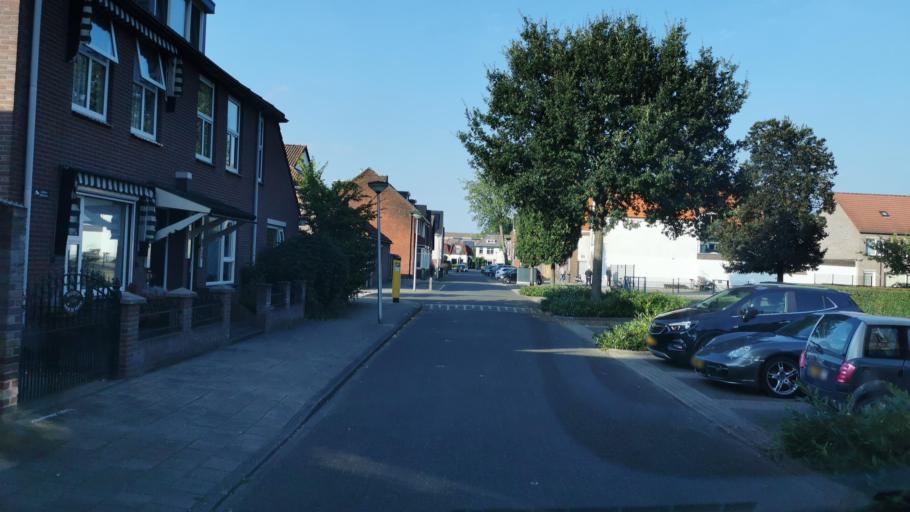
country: NL
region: Overijssel
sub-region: Gemeente Enschede
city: Enschede
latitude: 52.2123
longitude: 6.8931
